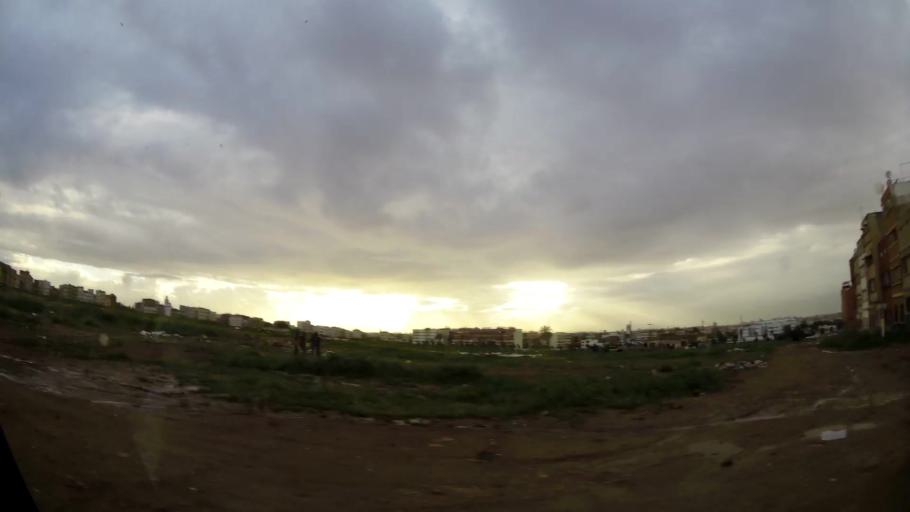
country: MA
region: Grand Casablanca
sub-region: Casablanca
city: Casablanca
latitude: 33.5571
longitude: -7.5751
